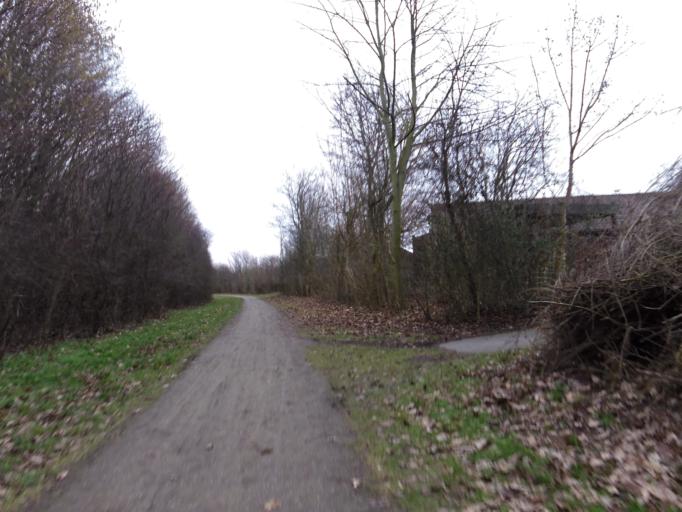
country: DK
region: South Denmark
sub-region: Odense Kommune
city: Neder Holluf
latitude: 55.3793
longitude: 10.4424
